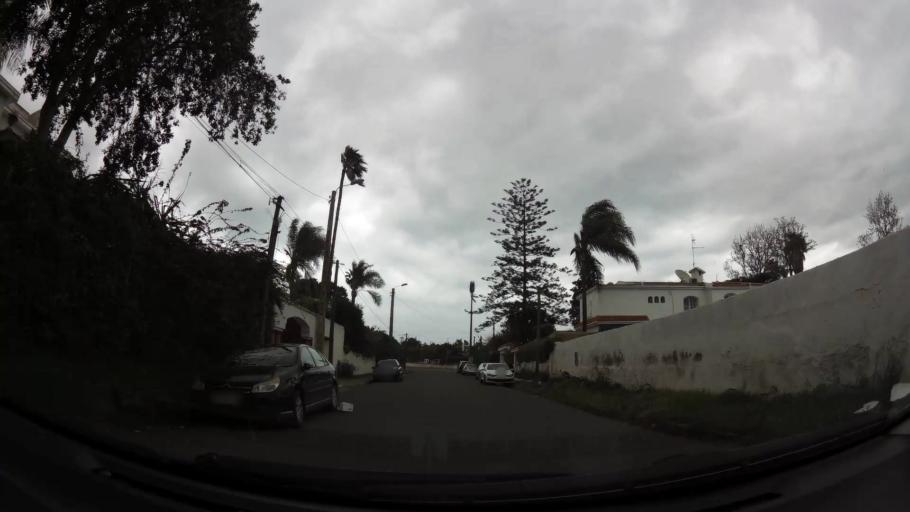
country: MA
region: Grand Casablanca
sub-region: Casablanca
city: Casablanca
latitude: 33.5820
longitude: -7.6662
